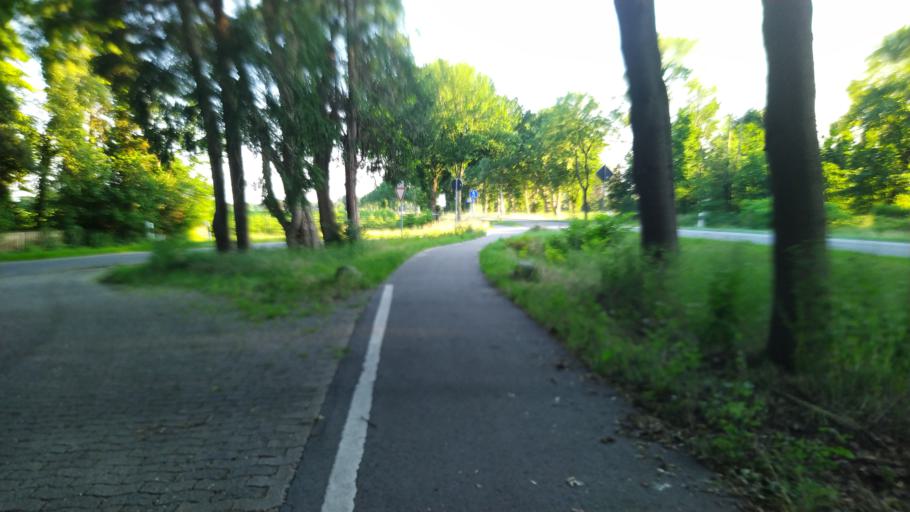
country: DE
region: Lower Saxony
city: Alfstedt
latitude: 53.5360
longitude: 9.0547
